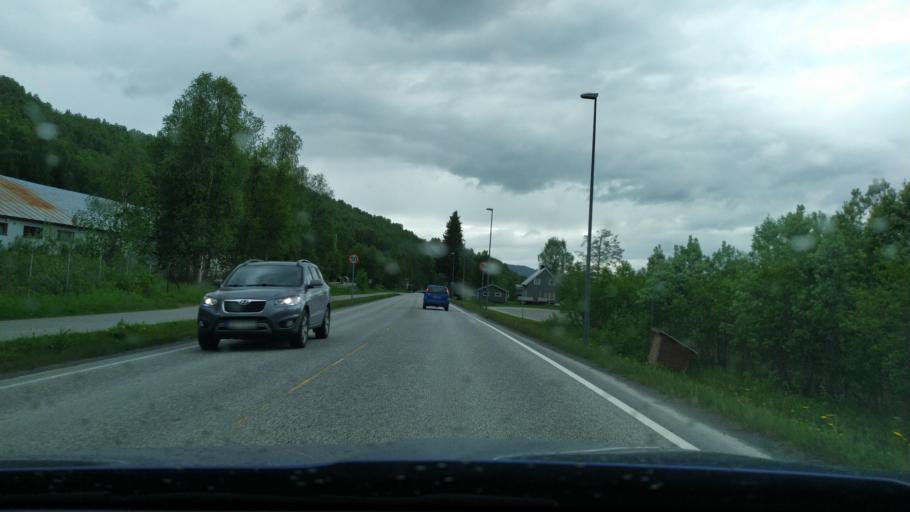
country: NO
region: Troms
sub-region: Malselv
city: Moen
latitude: 69.0292
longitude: 18.5017
